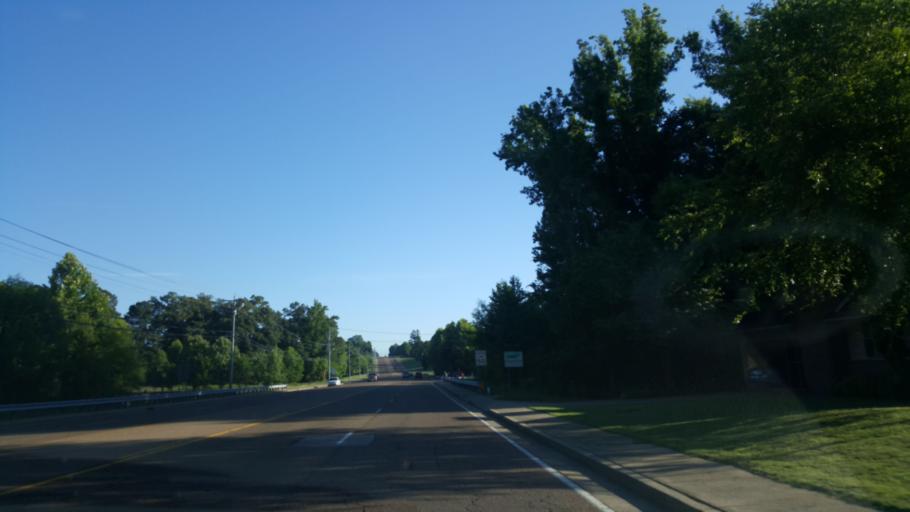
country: US
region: Tennessee
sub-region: Henderson County
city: Lexington
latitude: 35.6672
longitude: -88.3842
